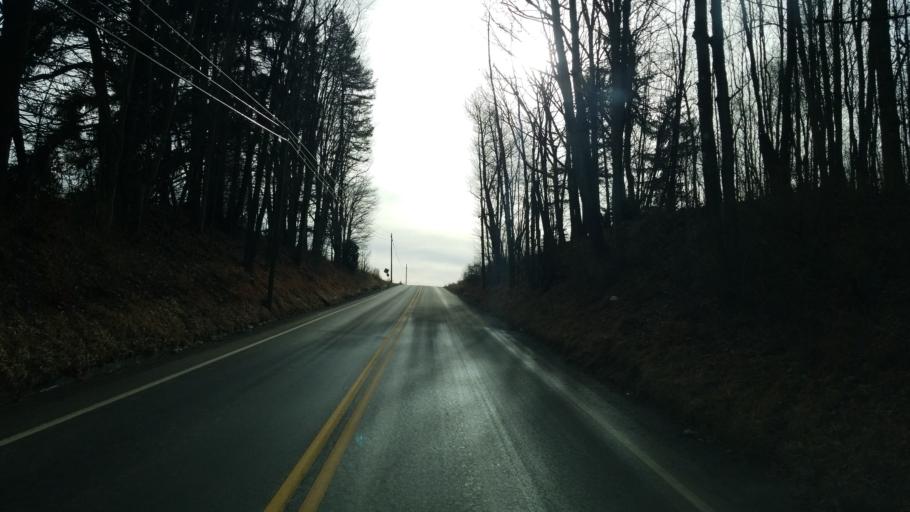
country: US
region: Pennsylvania
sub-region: Jefferson County
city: Punxsutawney
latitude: 40.8423
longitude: -79.0908
